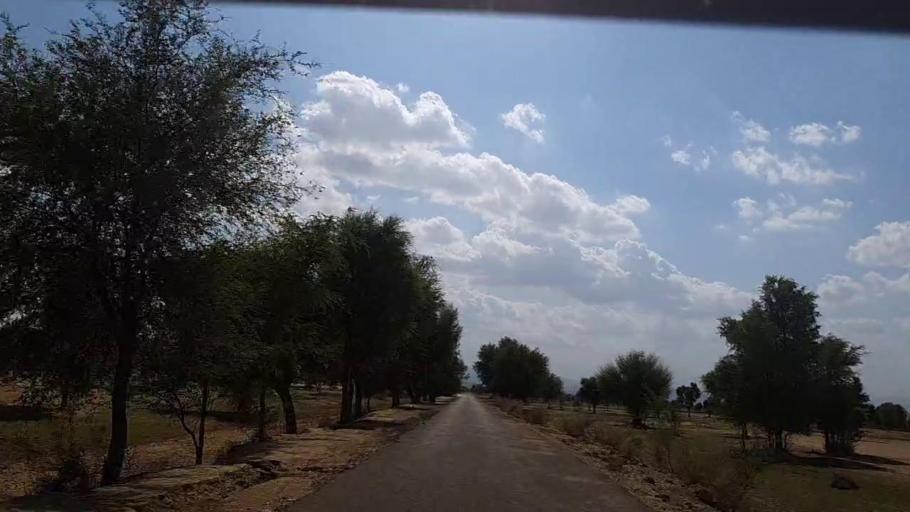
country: PK
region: Sindh
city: Johi
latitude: 26.5209
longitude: 67.4731
